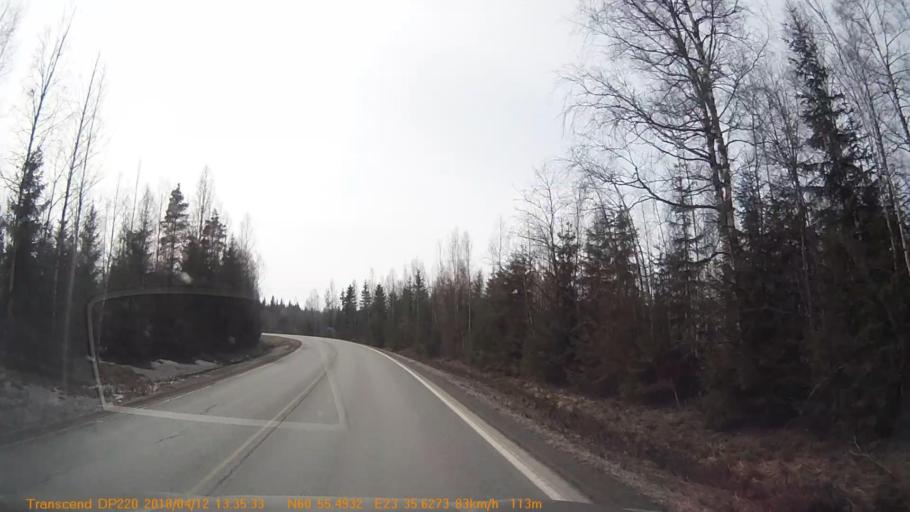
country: FI
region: Haeme
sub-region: Forssa
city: Forssa
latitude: 60.9247
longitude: 23.5932
